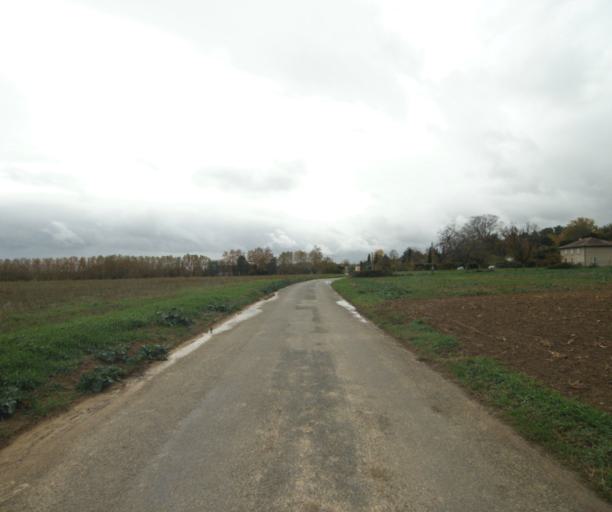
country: FR
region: Rhone-Alpes
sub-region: Departement de l'Ain
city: Pont-de-Vaux
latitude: 46.4626
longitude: 4.8873
